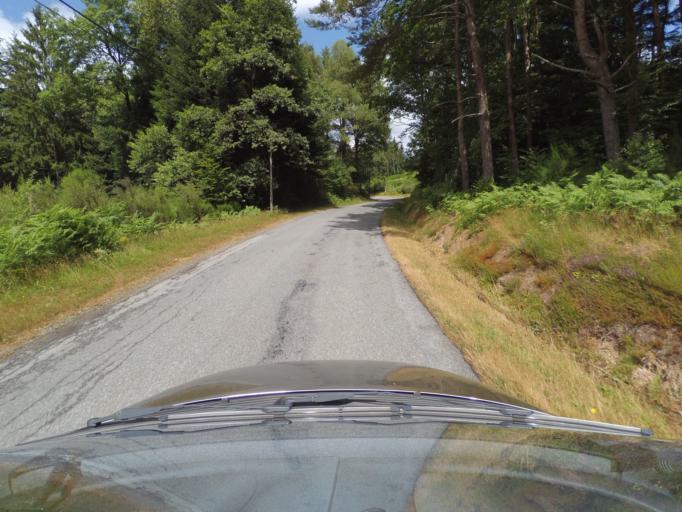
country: FR
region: Limousin
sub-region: Departement de la Creuse
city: Banize
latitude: 45.7664
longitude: 1.9466
